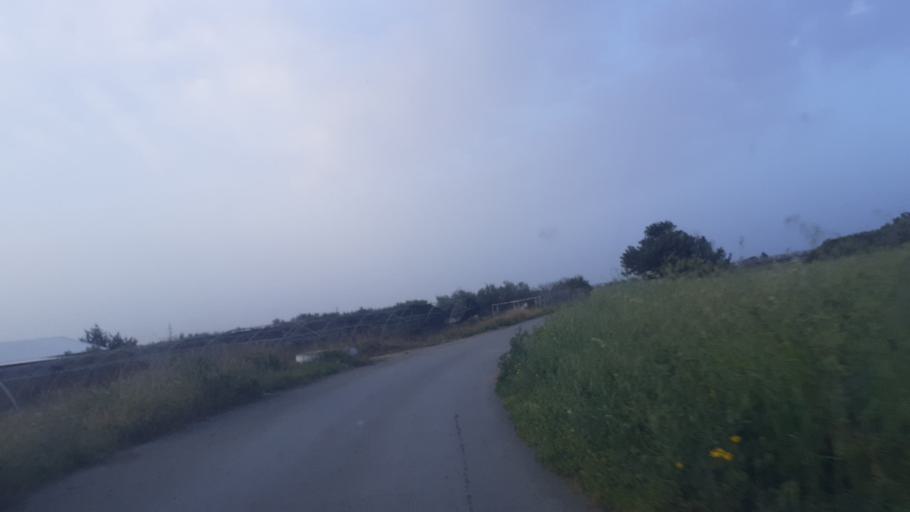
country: CY
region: Limassol
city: Ypsonas
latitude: 34.6735
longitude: 32.9705
